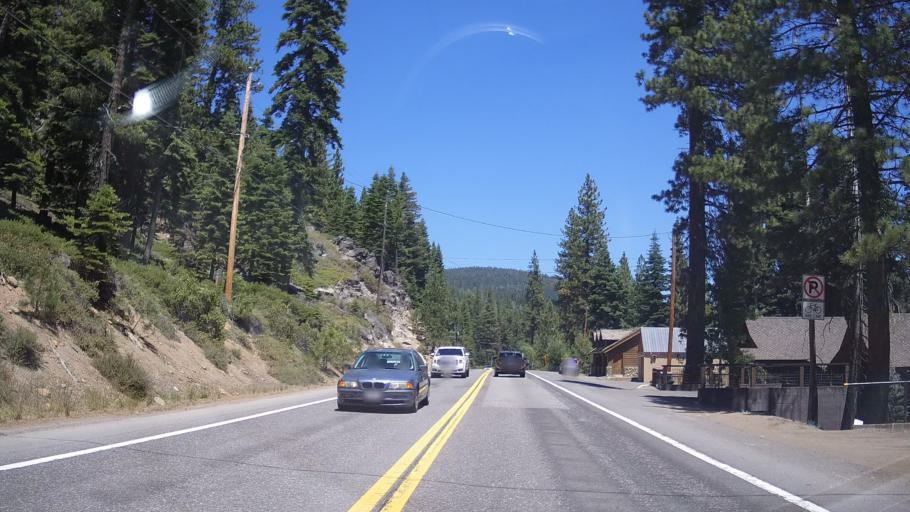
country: US
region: California
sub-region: Placer County
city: Dollar Point
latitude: 39.2208
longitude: -120.0869
